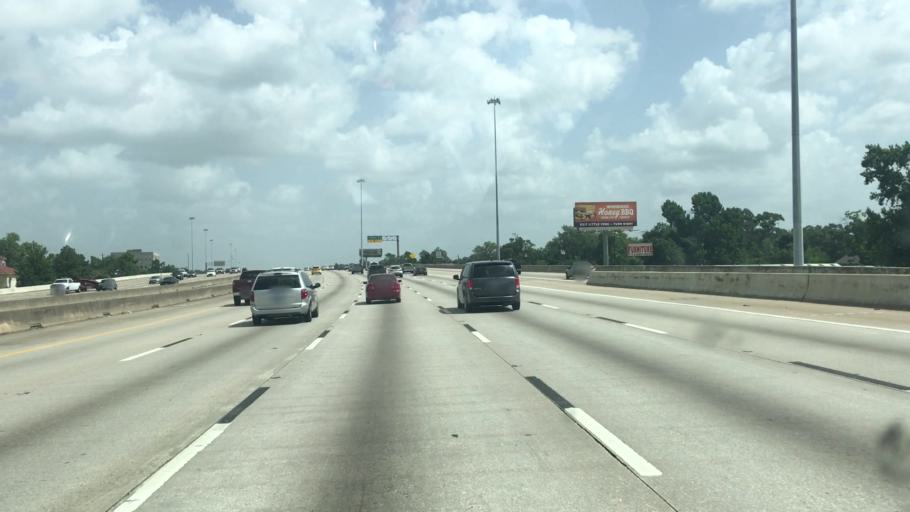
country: US
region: Texas
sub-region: Harris County
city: Houston
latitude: 29.8371
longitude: -95.3332
